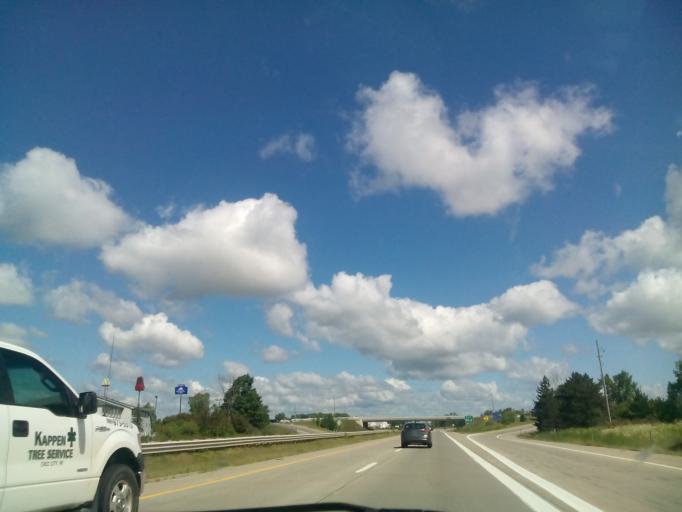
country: US
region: Michigan
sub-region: Genesee County
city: Flint
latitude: 42.9410
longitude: -83.7235
